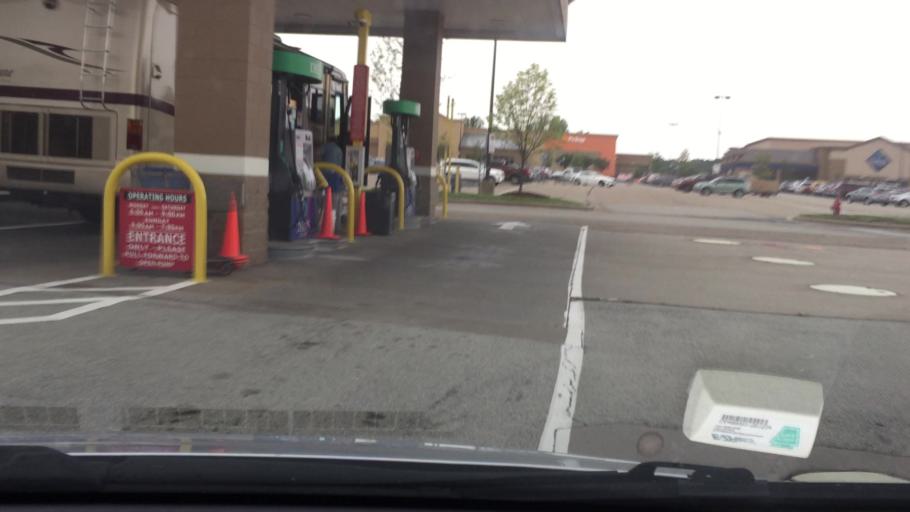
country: US
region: Pennsylvania
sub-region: Allegheny County
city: Cheswick
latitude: 40.5649
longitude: -79.8013
